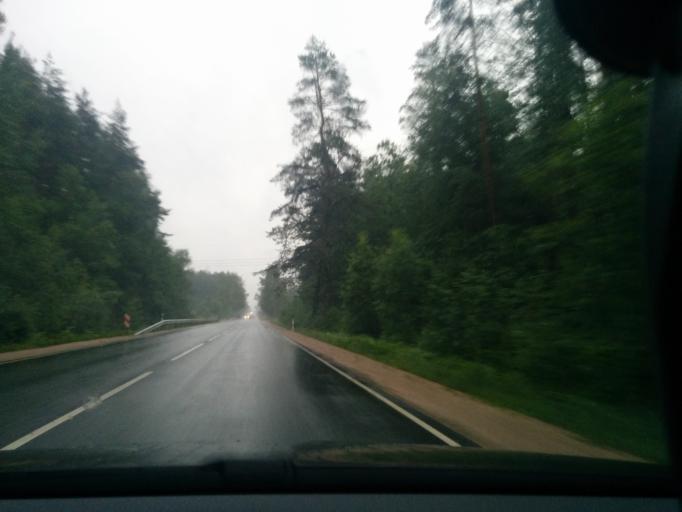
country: LV
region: Ikskile
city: Ikskile
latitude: 56.8892
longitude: 24.4823
